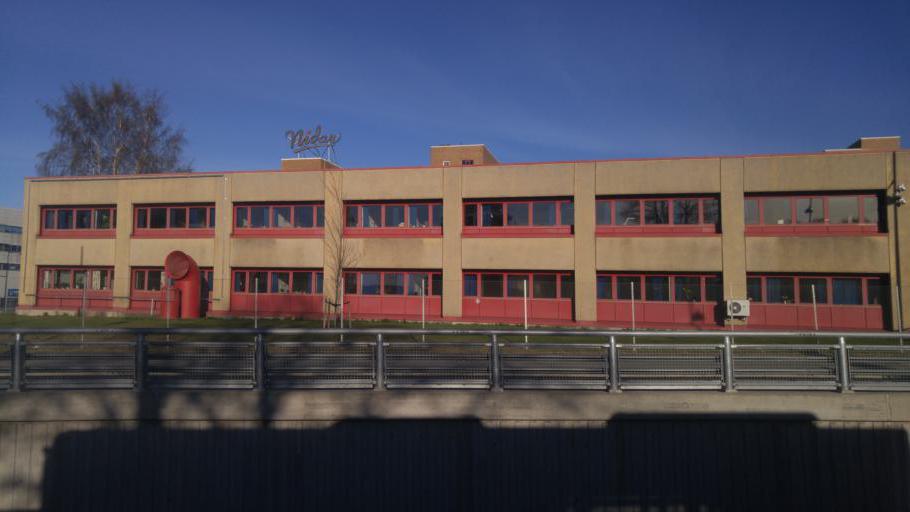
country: NO
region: Sor-Trondelag
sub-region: Trondheim
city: Trondheim
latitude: 63.4346
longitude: 10.4566
